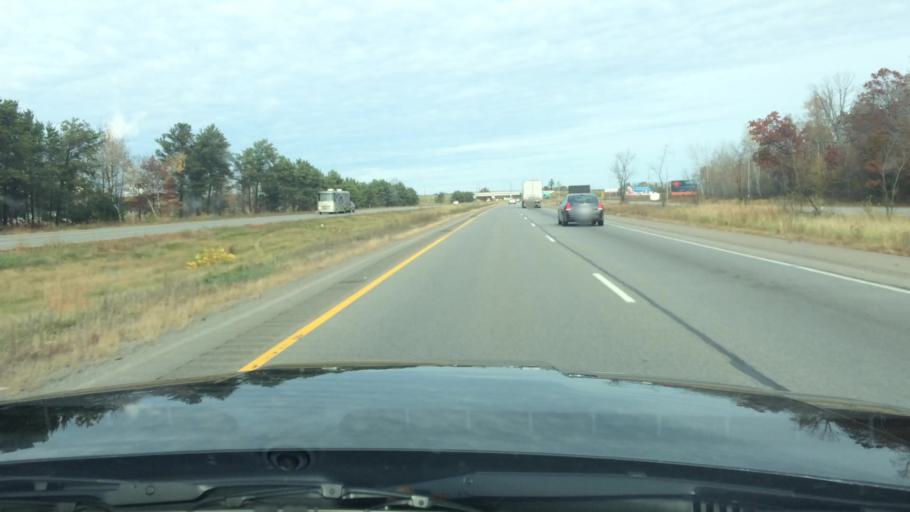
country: US
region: Wisconsin
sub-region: Marathon County
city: Evergreen
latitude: 44.8376
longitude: -89.6514
